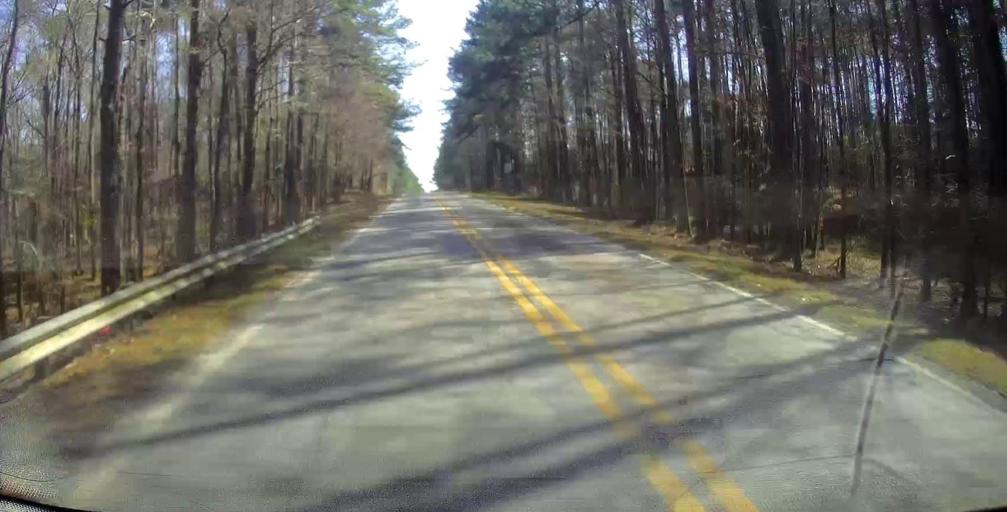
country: US
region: Georgia
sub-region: Jones County
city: Gray
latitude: 32.9251
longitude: -83.5318
